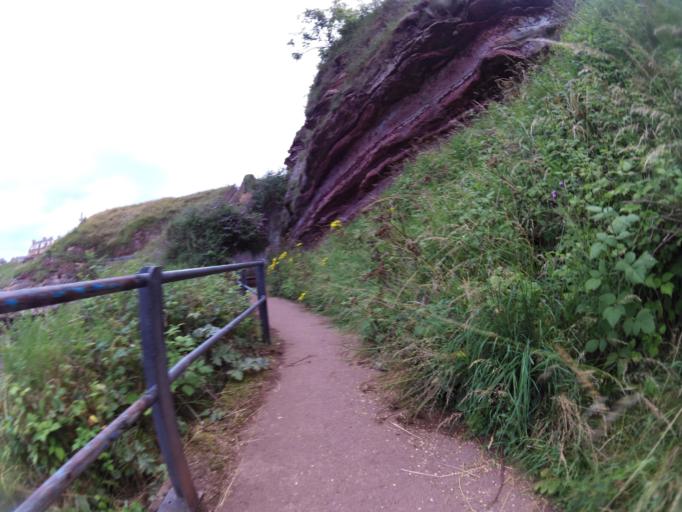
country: GB
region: Scotland
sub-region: East Lothian
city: Dunbar
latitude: 56.0050
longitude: -2.5219
